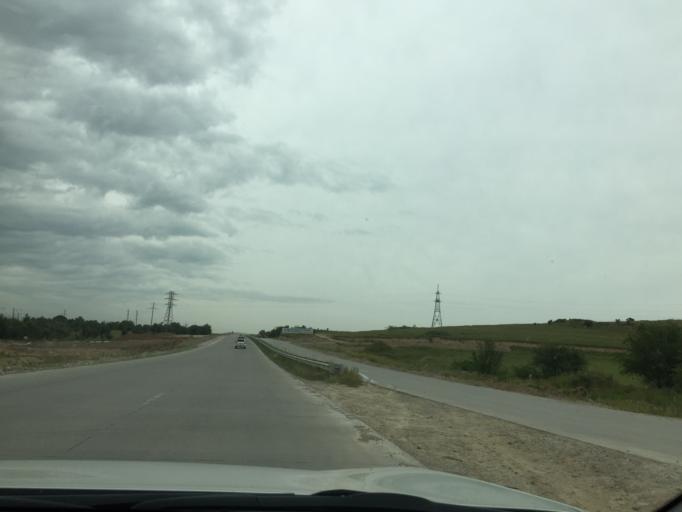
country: KZ
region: Ongtustik Qazaqstan
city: Sastobe
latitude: 42.5315
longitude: 70.0206
